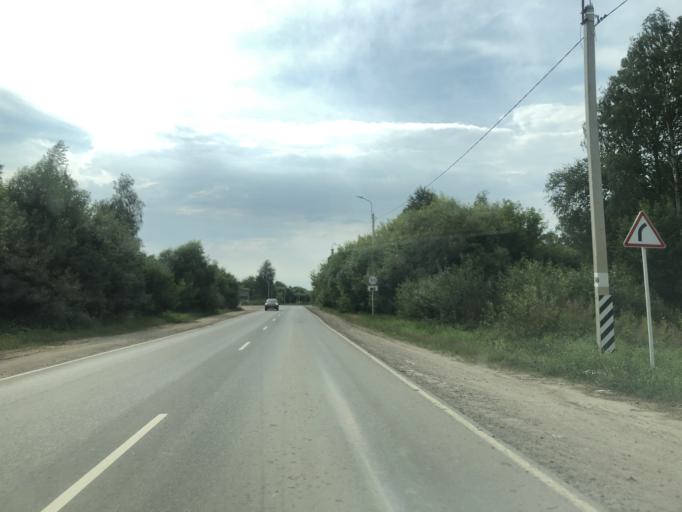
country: RU
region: Ivanovo
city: Shuya
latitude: 56.8535
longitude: 41.5548
